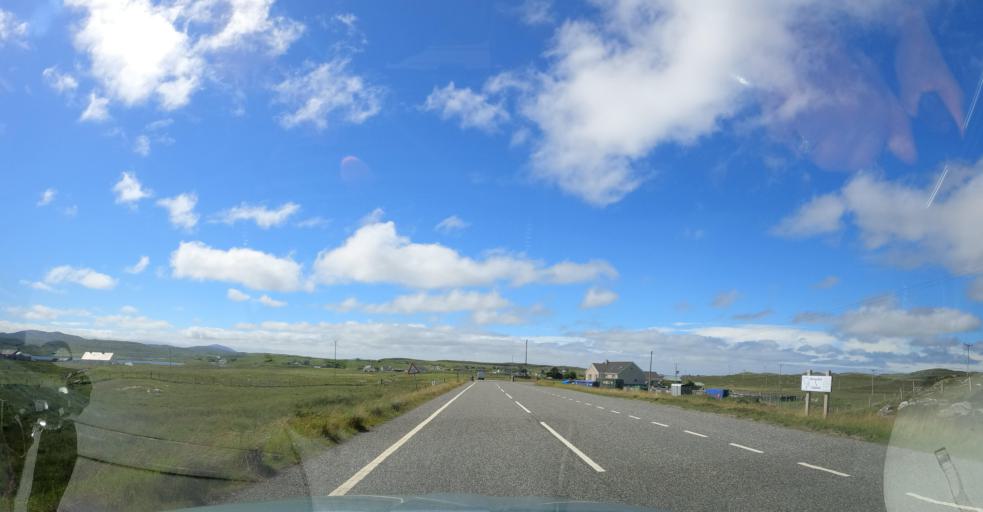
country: GB
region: Scotland
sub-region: Eilean Siar
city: Harris
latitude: 58.1976
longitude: -6.7254
